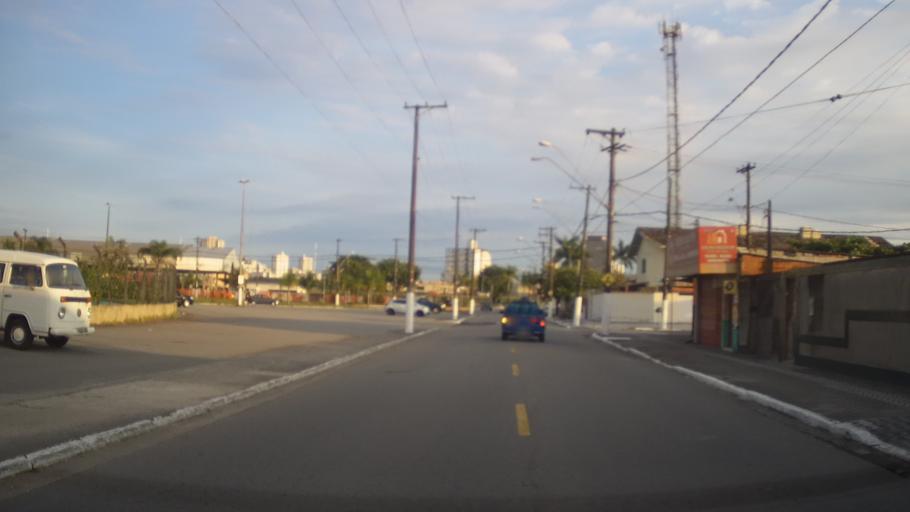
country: BR
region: Sao Paulo
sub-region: Praia Grande
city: Praia Grande
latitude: -23.9979
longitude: -46.4159
